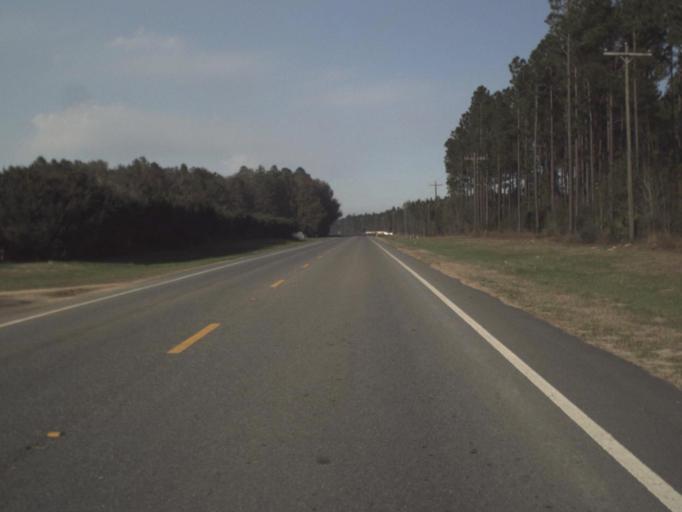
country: US
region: Florida
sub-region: Calhoun County
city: Blountstown
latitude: 30.5184
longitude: -85.1968
